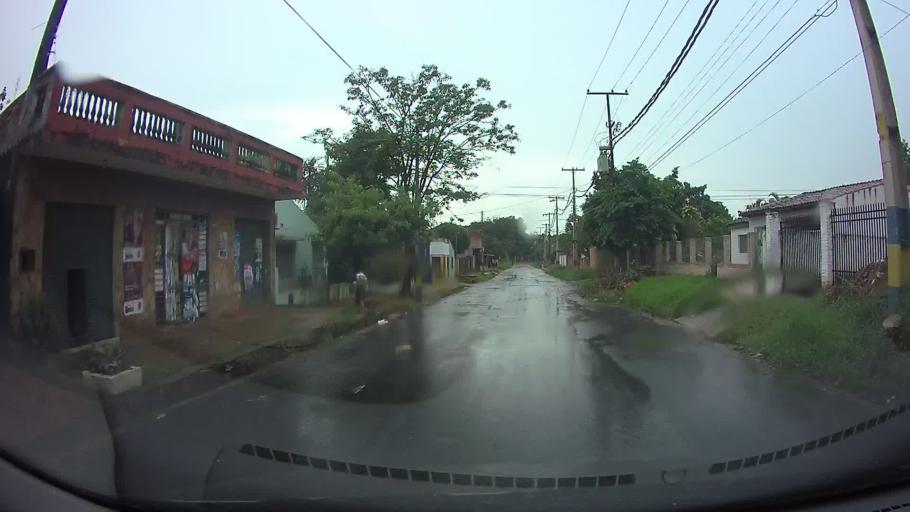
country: PY
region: Central
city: San Lorenzo
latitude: -25.2682
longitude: -57.4788
